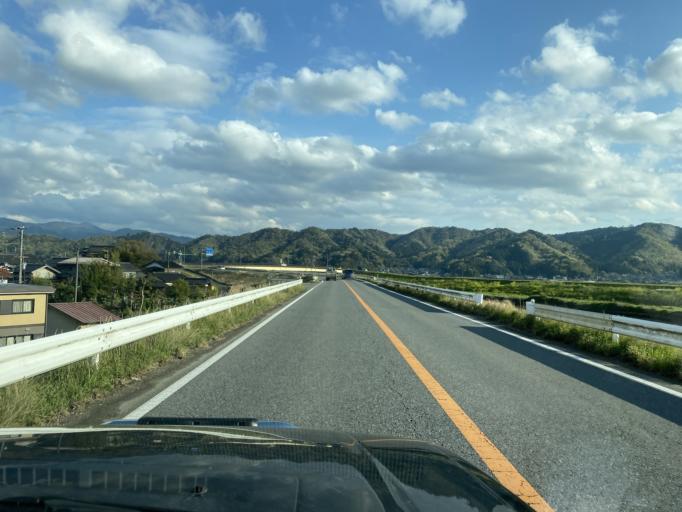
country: JP
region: Hyogo
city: Toyooka
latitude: 35.4947
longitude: 134.8406
